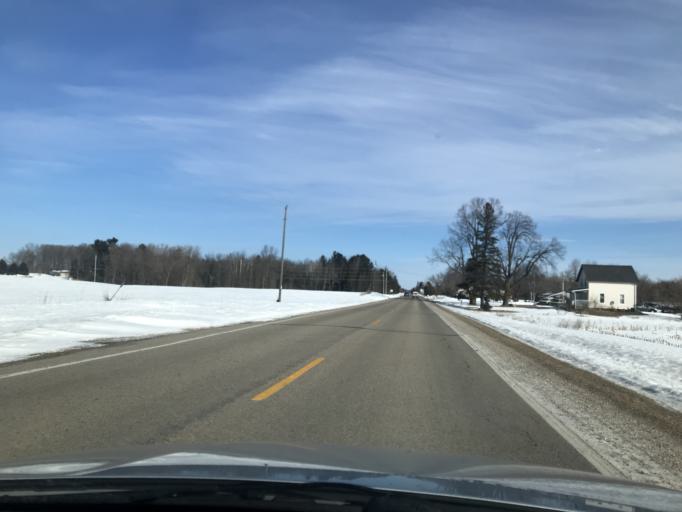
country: US
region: Wisconsin
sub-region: Oconto County
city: Oconto Falls
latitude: 44.9057
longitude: -88.1553
